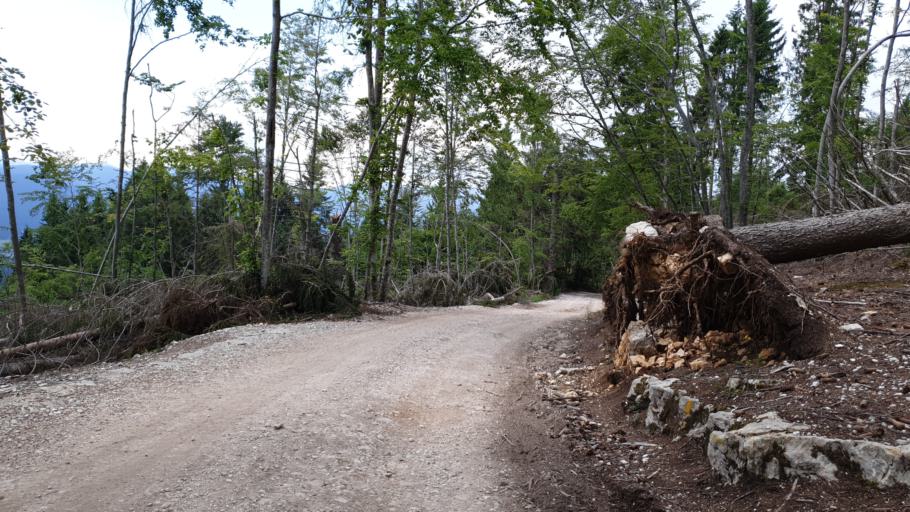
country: IT
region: Veneto
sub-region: Provincia di Vicenza
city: Canove di Roana
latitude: 45.8957
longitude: 11.4817
